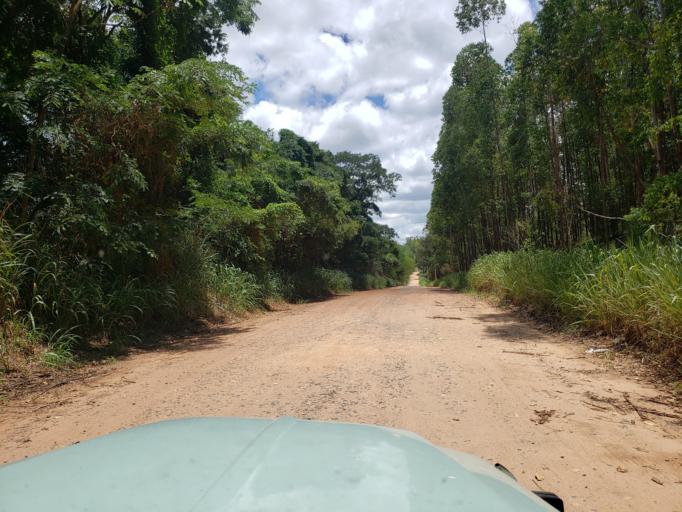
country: BR
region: Sao Paulo
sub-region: Moji-Guacu
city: Mogi-Gaucu
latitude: -22.2532
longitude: -46.8490
